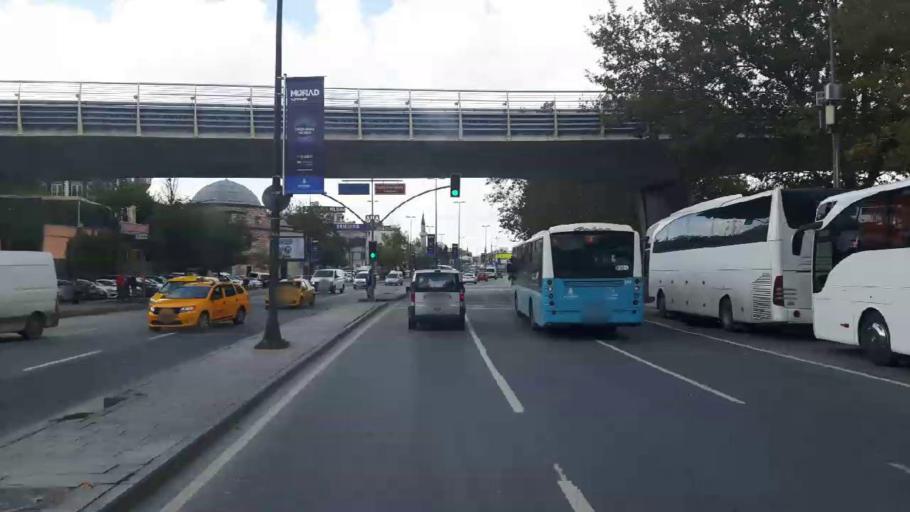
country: TR
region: Istanbul
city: Eminoenue
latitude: 41.0198
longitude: 28.9646
